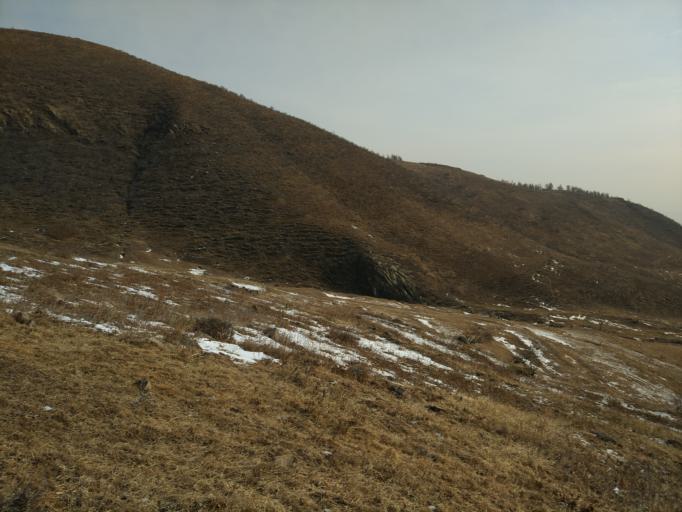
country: CN
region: Hebei
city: Xiwanzi
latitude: 40.8567
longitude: 115.4556
